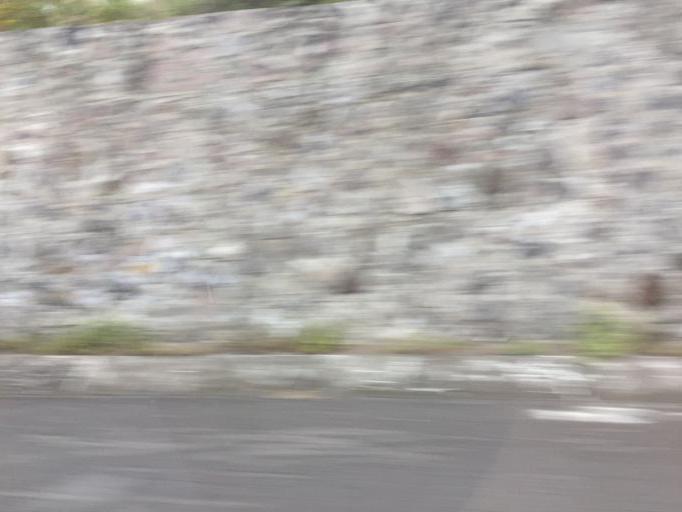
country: MX
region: Michoacan
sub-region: Puruandiro
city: San Lorenzo
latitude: 19.9563
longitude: -101.6609
